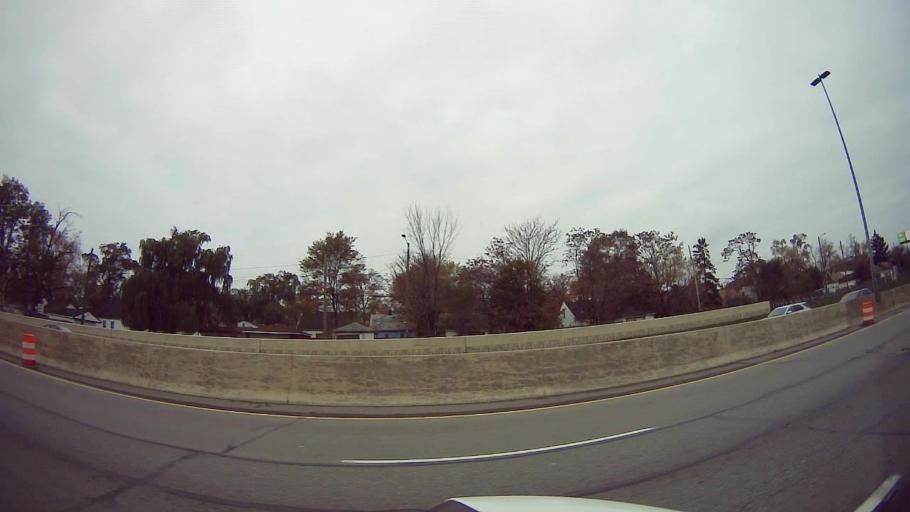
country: US
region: Michigan
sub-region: Wayne County
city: Dearborn Heights
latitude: 42.3847
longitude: -83.2174
